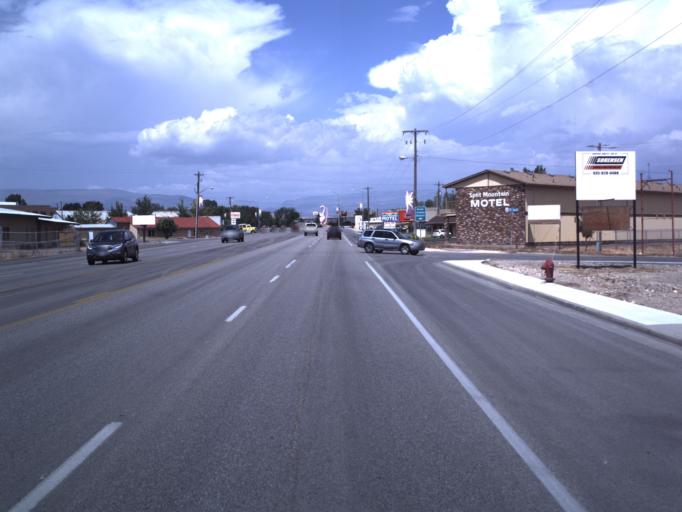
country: US
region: Utah
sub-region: Uintah County
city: Vernal
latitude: 40.4535
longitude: -109.5080
